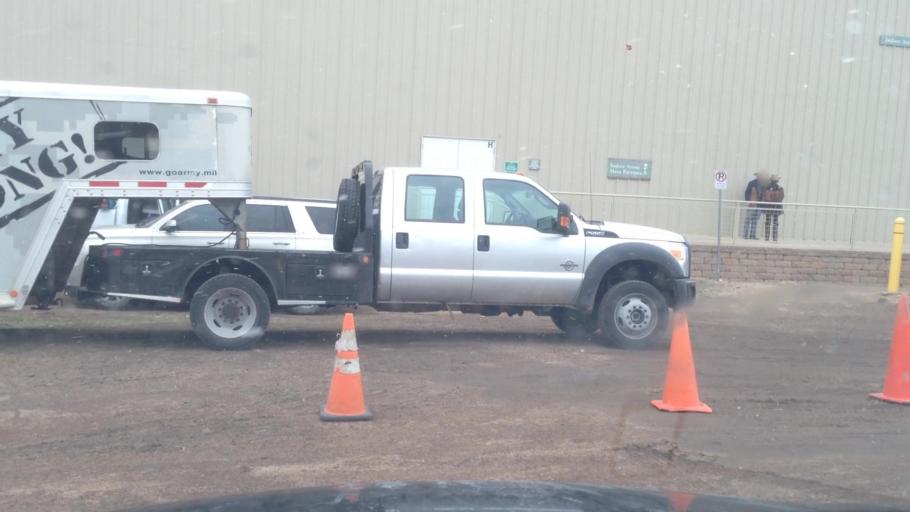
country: US
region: Colorado
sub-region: Douglas County
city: Castle Rock
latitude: 39.3652
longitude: -104.8540
